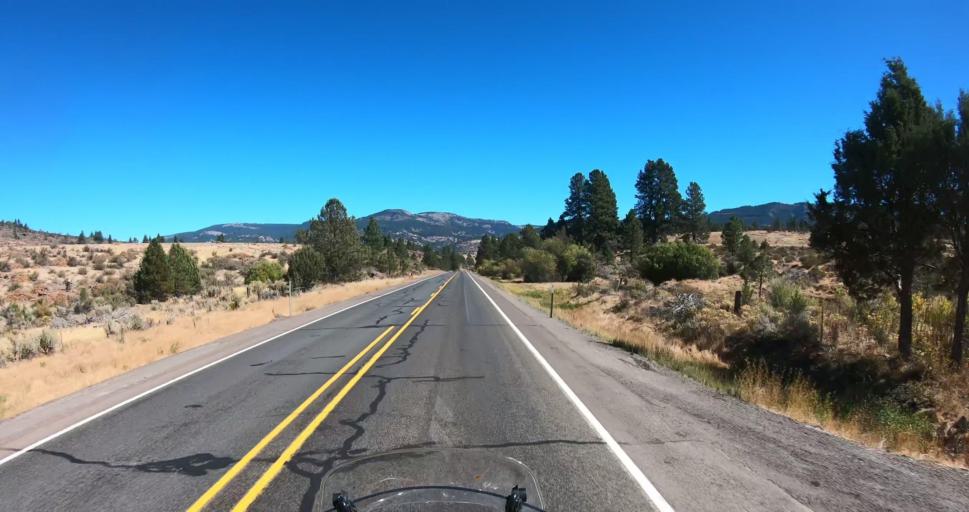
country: US
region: Oregon
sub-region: Lake County
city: Lakeview
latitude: 42.3244
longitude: -120.3175
